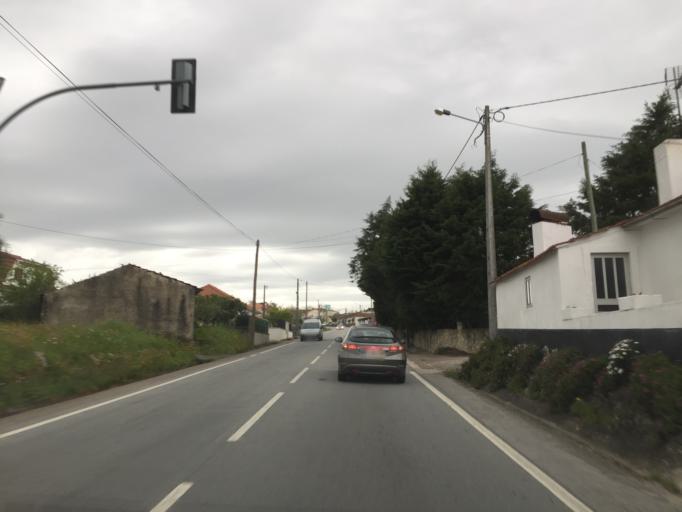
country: PT
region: Leiria
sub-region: Leiria
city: Santa Catarina da Serra
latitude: 39.6777
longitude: -8.6729
